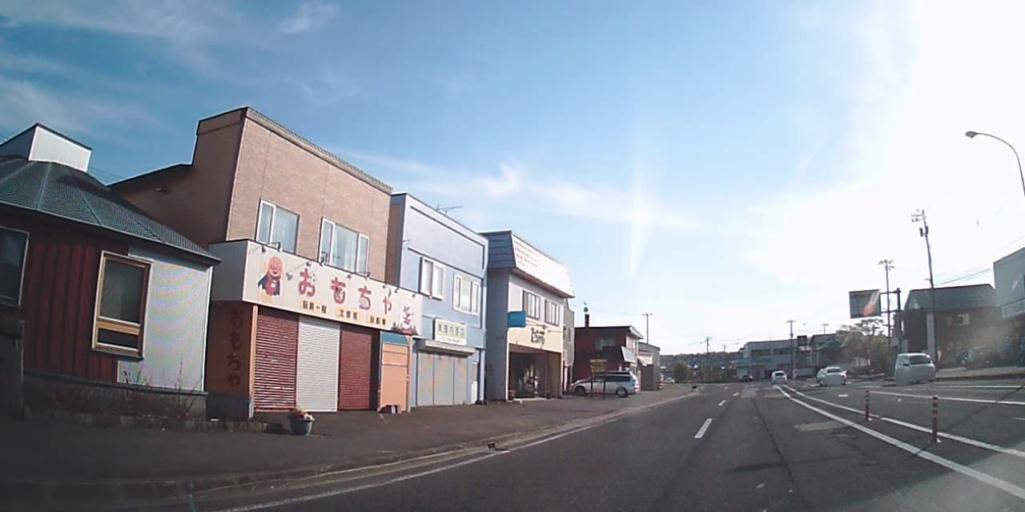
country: JP
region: Hokkaido
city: Shiraoi
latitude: 42.4543
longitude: 141.1777
